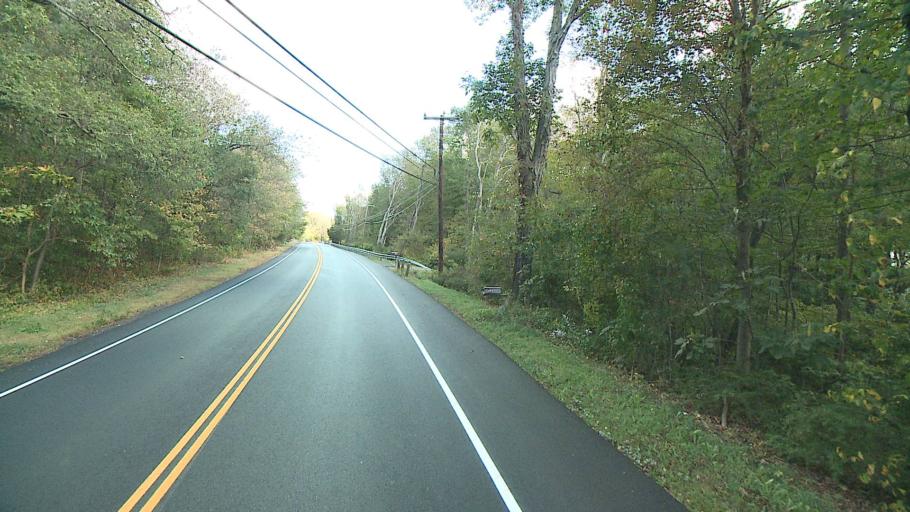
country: US
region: Connecticut
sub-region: New Haven County
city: Prospect
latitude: 41.4567
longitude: -72.9804
